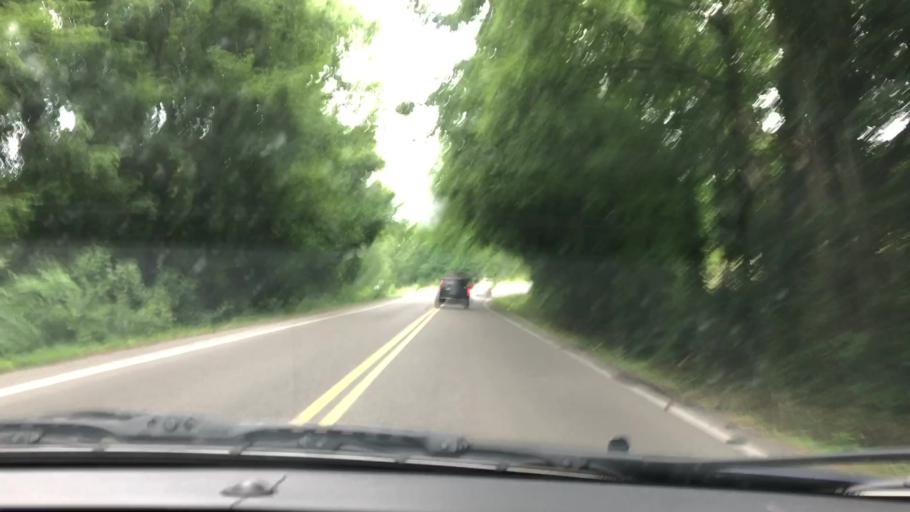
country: US
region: Tennessee
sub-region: Maury County
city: Columbia
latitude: 35.7021
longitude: -87.0157
